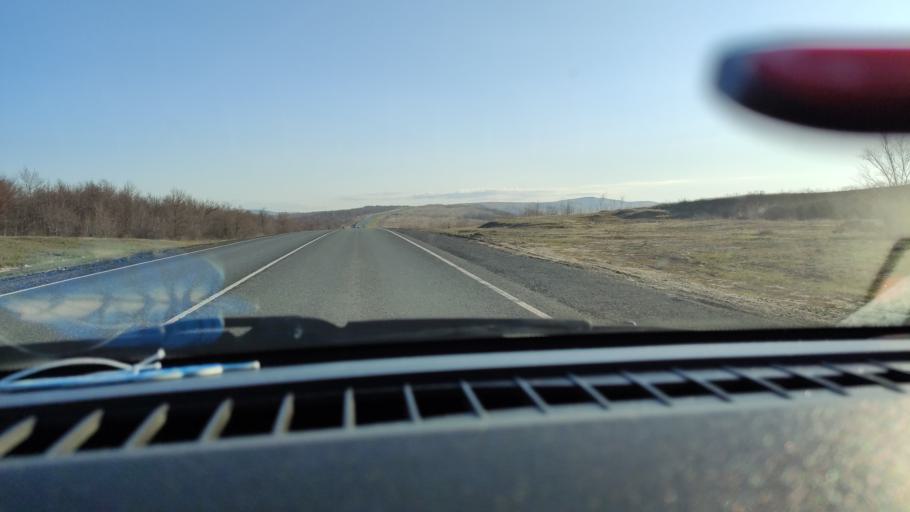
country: RU
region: Saratov
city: Balakovo
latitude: 52.1930
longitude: 47.8557
